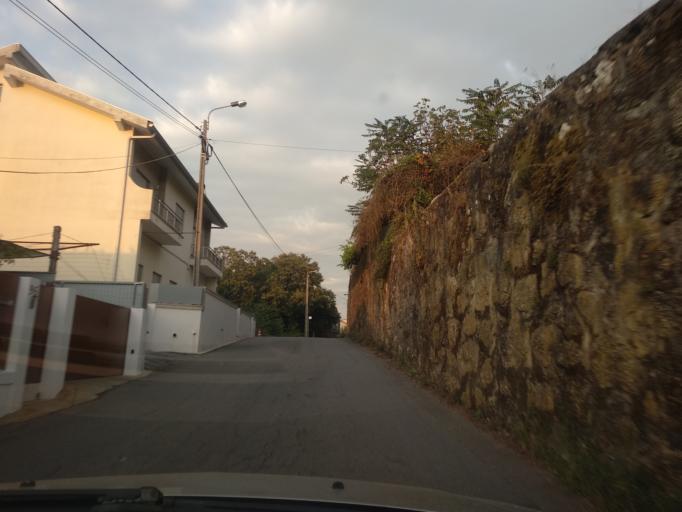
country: PT
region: Braga
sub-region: Braga
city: Braga
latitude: 41.5299
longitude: -8.4486
